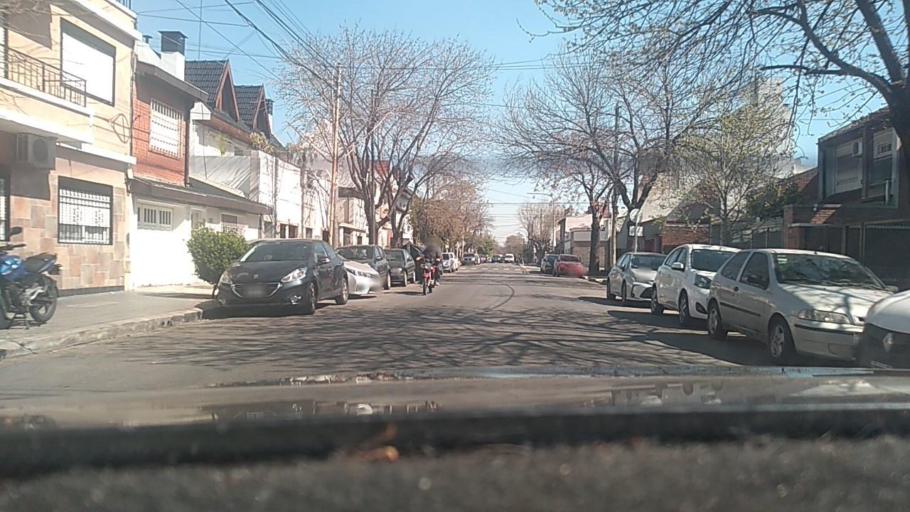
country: AR
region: Buenos Aires F.D.
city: Villa Santa Rita
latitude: -34.6110
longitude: -58.5009
